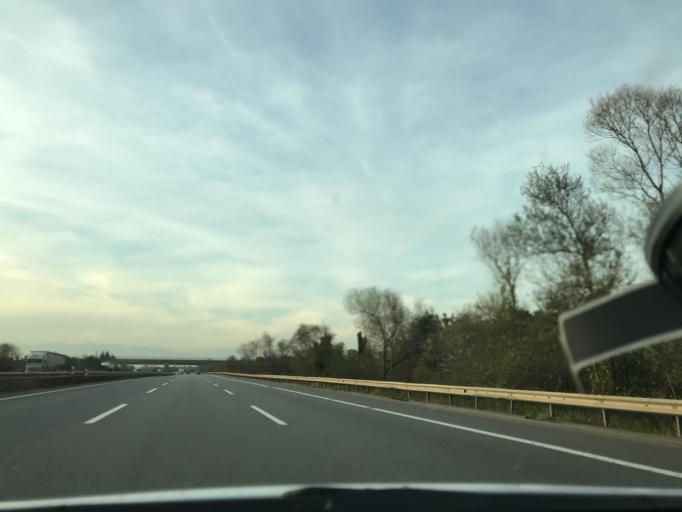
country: TR
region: Duzce
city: Cilimli
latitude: 40.8405
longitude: 31.0261
